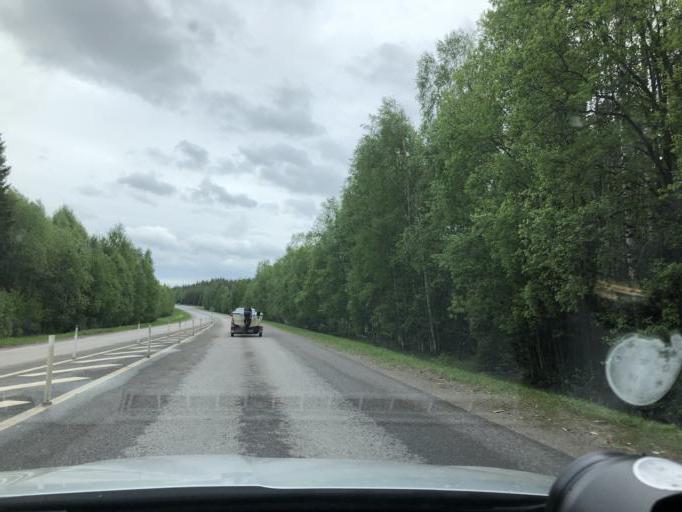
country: SE
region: Norrbotten
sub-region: Pitea Kommun
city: Pitea
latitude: 65.2809
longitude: 21.5103
